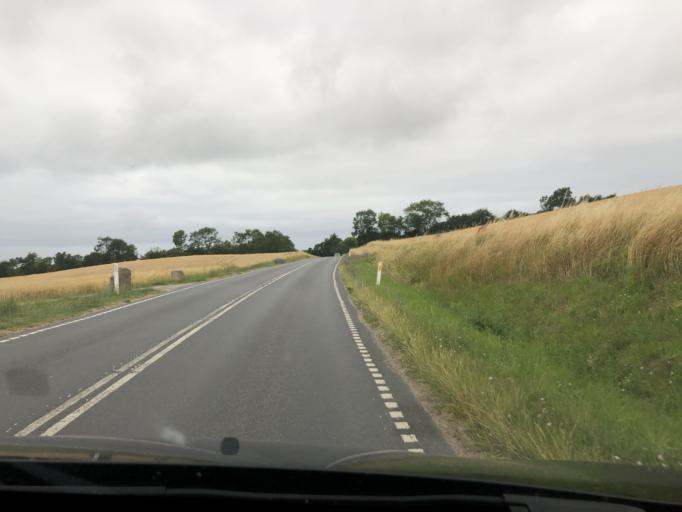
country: DK
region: South Denmark
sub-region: AEro Kommune
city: AEroskobing
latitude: 54.9065
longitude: 10.2928
